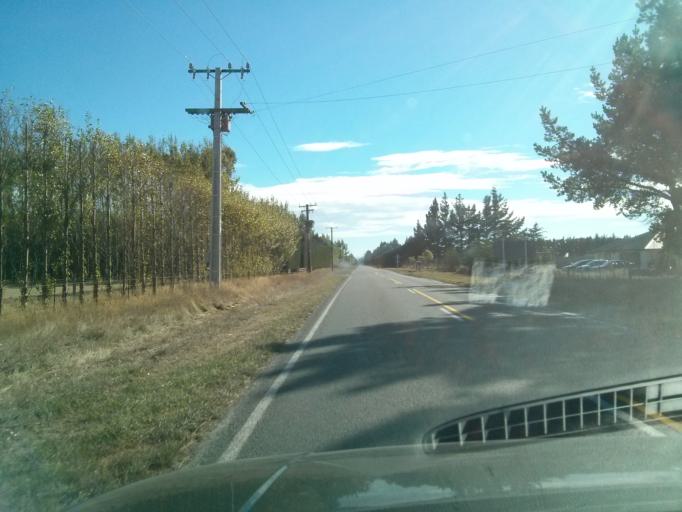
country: NZ
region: Canterbury
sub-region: Waimakariri District
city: Kaiapoi
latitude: -43.3662
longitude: 172.4898
